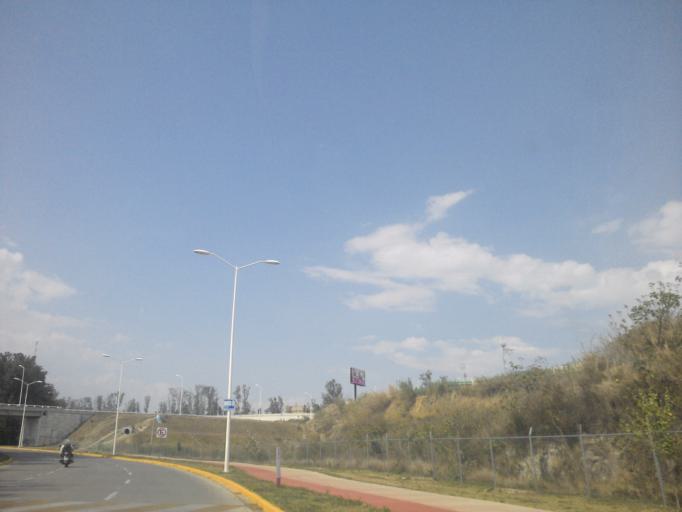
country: MX
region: Jalisco
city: Zapopan2
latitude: 20.6876
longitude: -103.4579
